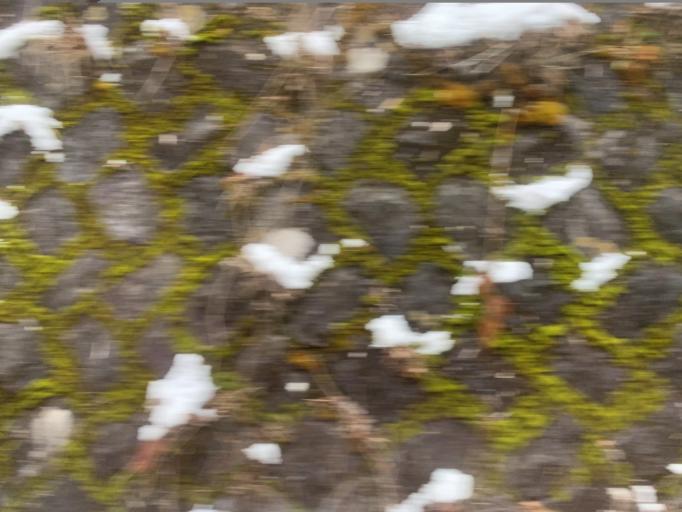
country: JP
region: Gifu
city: Takayama
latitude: 35.9913
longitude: 137.2769
